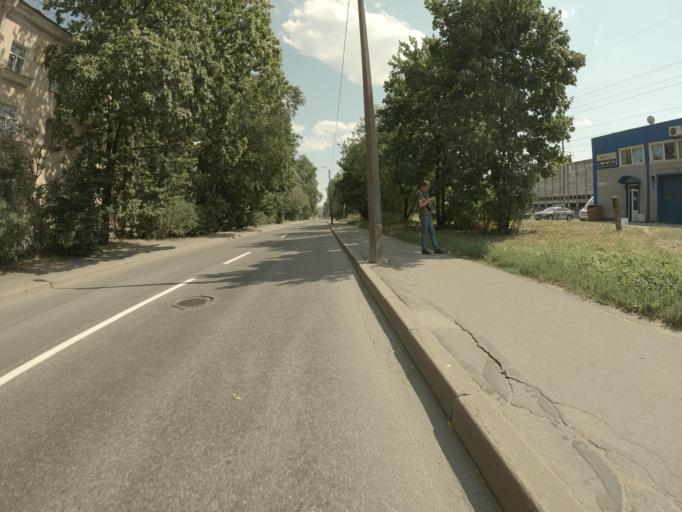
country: RU
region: St.-Petersburg
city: Avtovo
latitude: 59.8890
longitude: 30.2610
